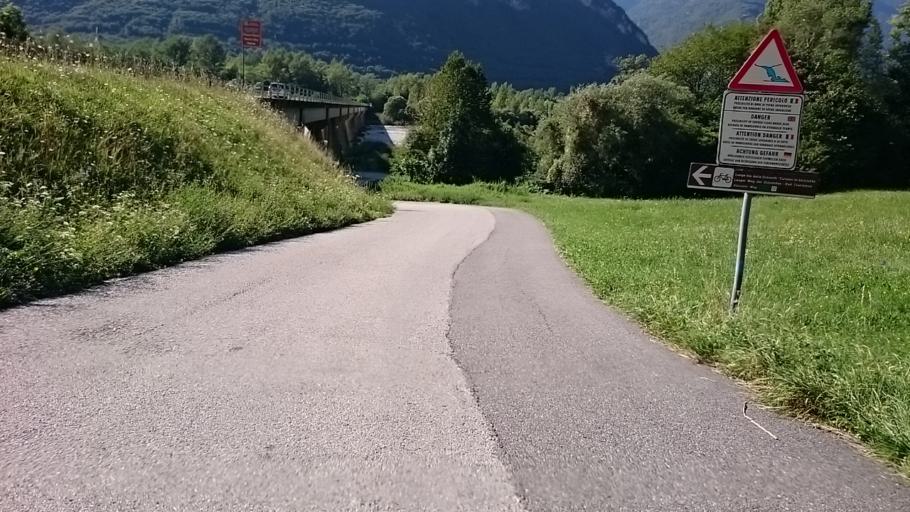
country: IT
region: Veneto
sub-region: Provincia di Belluno
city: Longarone
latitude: 46.2421
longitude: 12.3090
